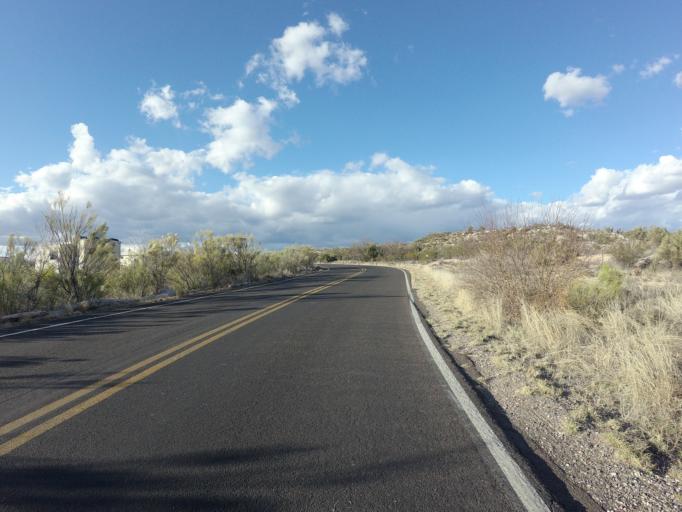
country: US
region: Arizona
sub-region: Yavapai County
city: Cottonwood
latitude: 34.7609
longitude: -112.0147
